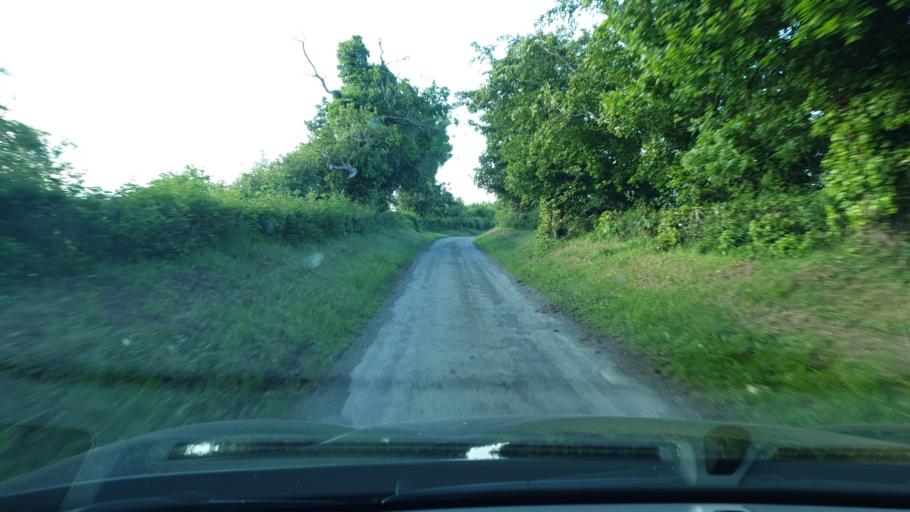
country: IE
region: Leinster
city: Hartstown
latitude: 53.4503
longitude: -6.4103
